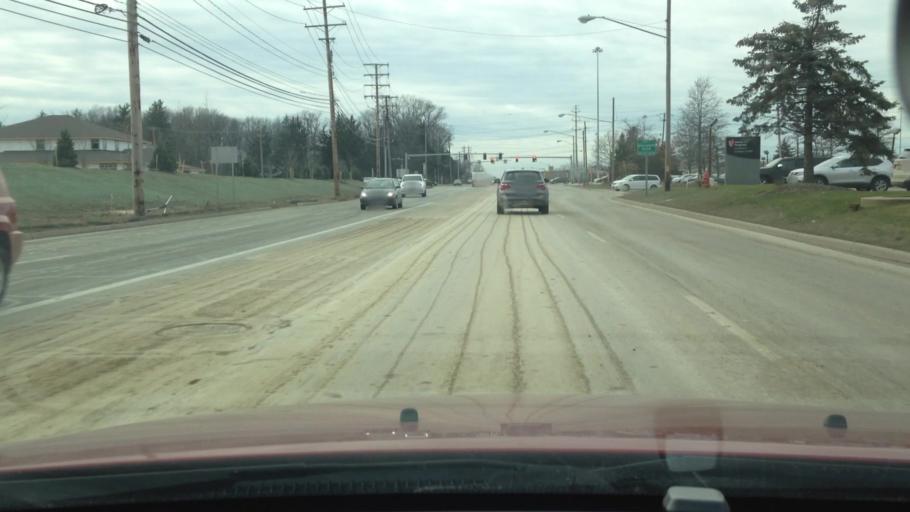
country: US
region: Ohio
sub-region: Cuyahoga County
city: Lyndhurst
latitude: 41.5012
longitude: -81.4741
